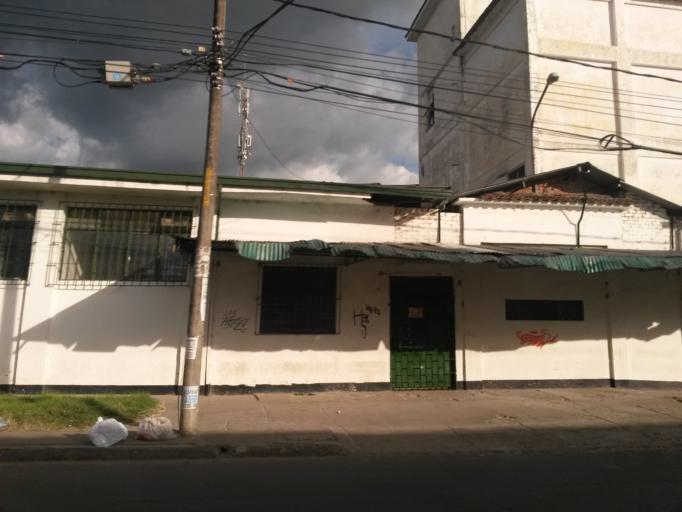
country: CO
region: Cauca
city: Popayan
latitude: 2.4544
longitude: -76.6033
